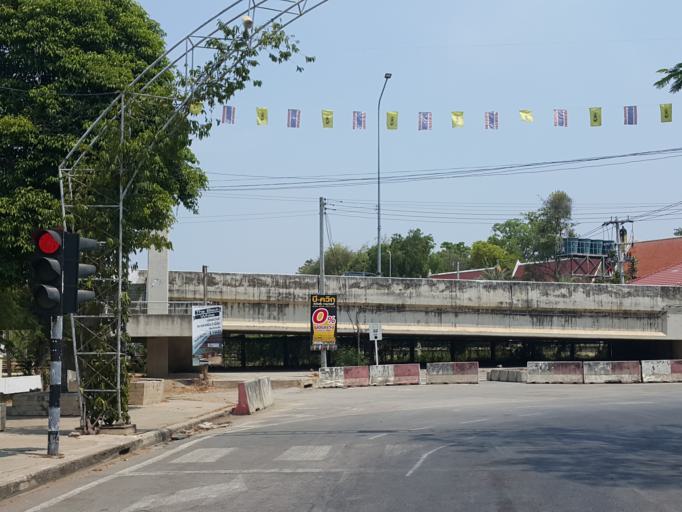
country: TH
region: Kanchanaburi
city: Kanchanaburi
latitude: 14.0252
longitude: 99.5262
